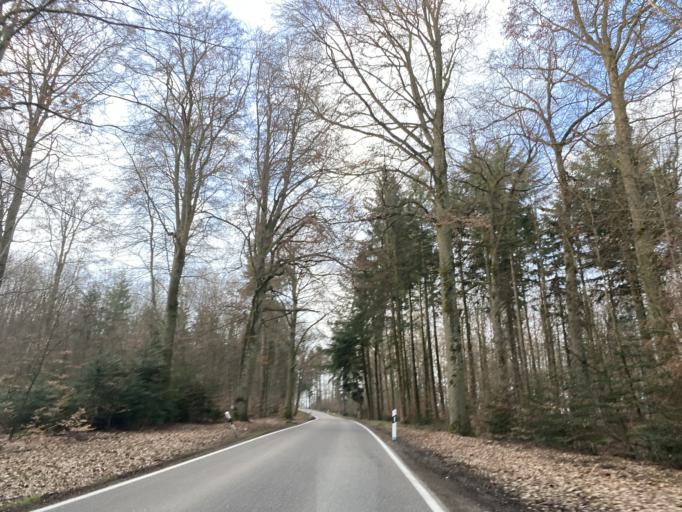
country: DE
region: Baden-Wuerttemberg
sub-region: Karlsruhe Region
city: Wiernsheim
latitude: 48.9010
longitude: 8.8832
